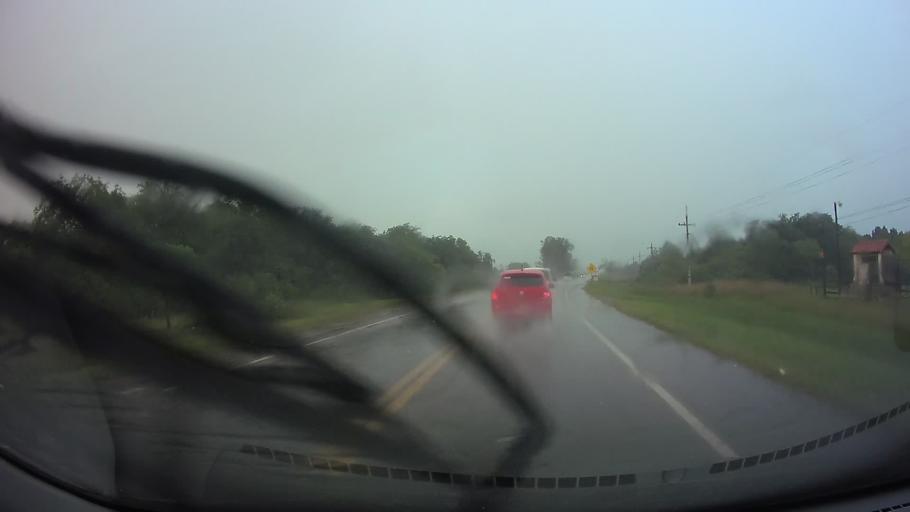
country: PY
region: Paraguari
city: Paraguari
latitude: -25.6475
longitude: -57.1587
